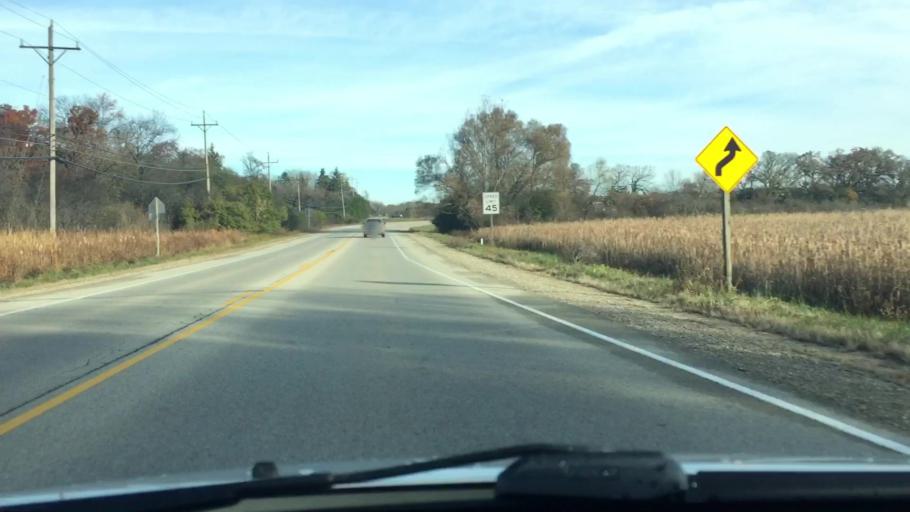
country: US
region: Wisconsin
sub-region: Waukesha County
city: Hartland
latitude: 43.0890
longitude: -88.3631
